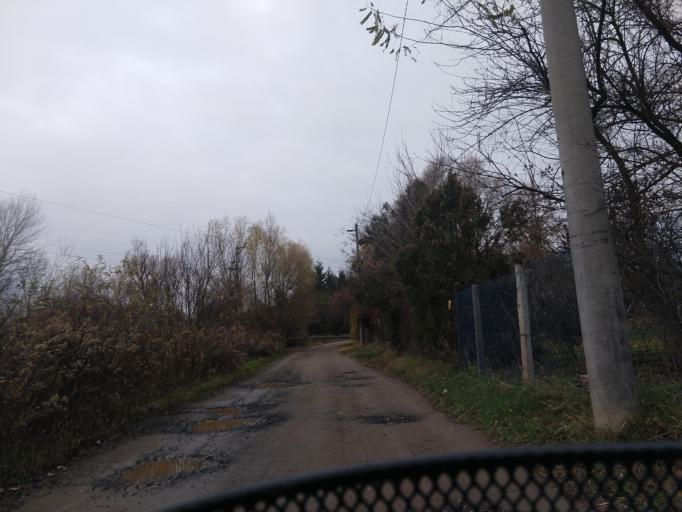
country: HU
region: Pest
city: Orbottyan
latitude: 47.6767
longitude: 19.2863
